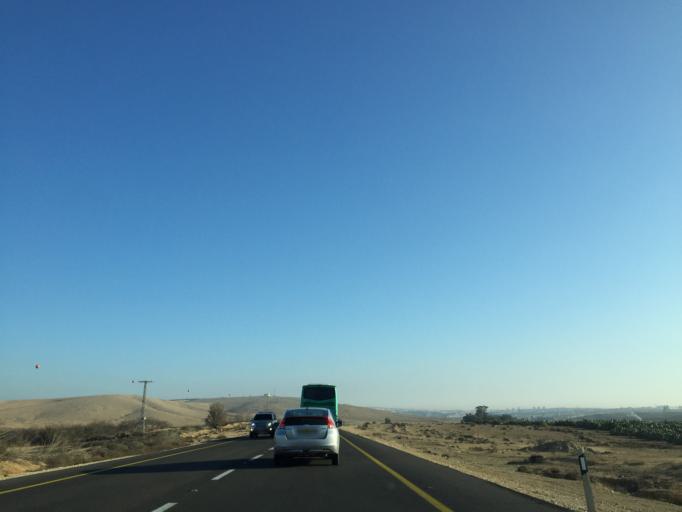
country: IL
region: Southern District
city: Dimona
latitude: 31.0449
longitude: 34.9817
